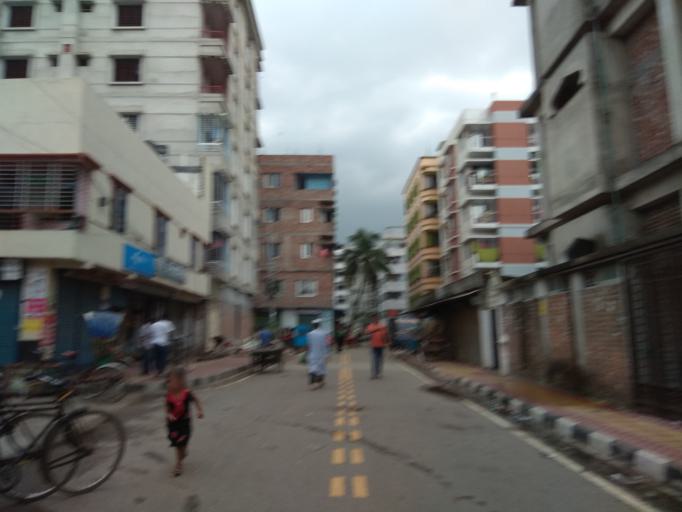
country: BD
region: Dhaka
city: Tungi
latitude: 23.8217
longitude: 90.3718
